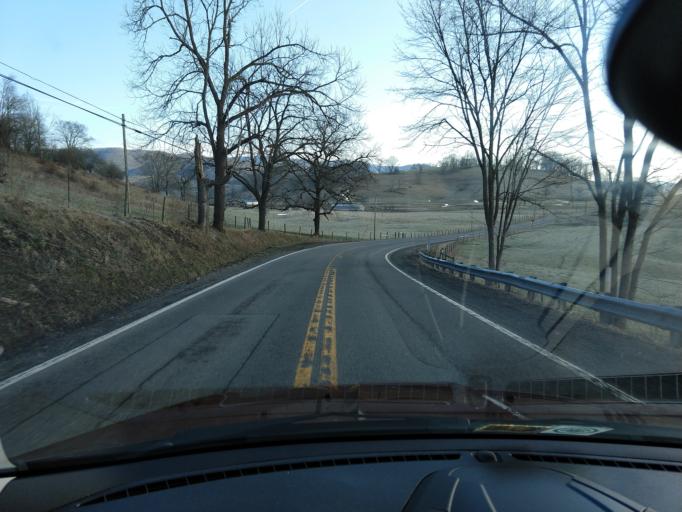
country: US
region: West Virginia
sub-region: Pocahontas County
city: Marlinton
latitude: 38.1241
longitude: -80.2366
